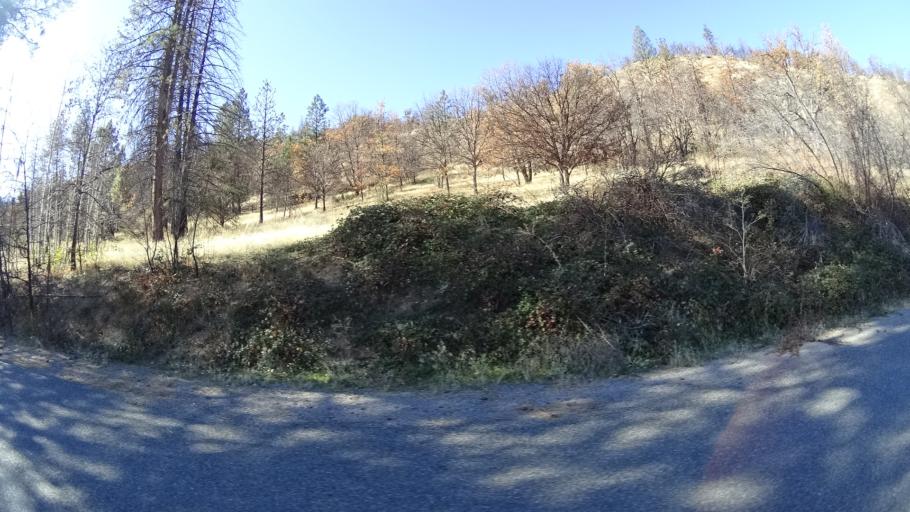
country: US
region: California
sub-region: Siskiyou County
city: Yreka
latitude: 41.9369
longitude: -122.5919
